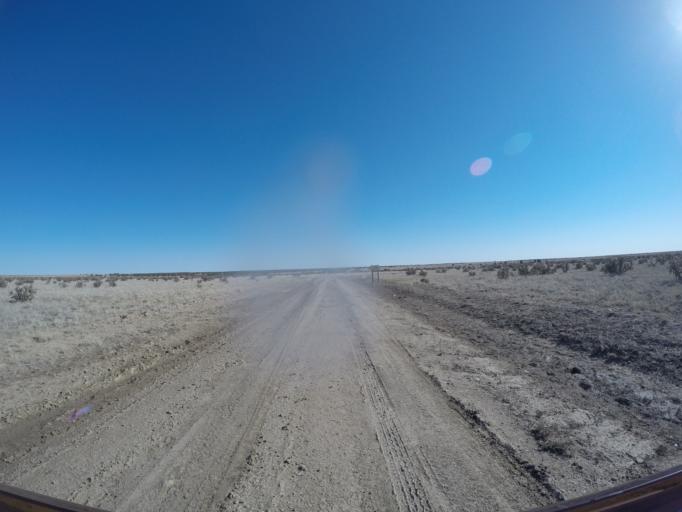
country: US
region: Colorado
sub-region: Otero County
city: La Junta
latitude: 37.6594
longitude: -103.6126
